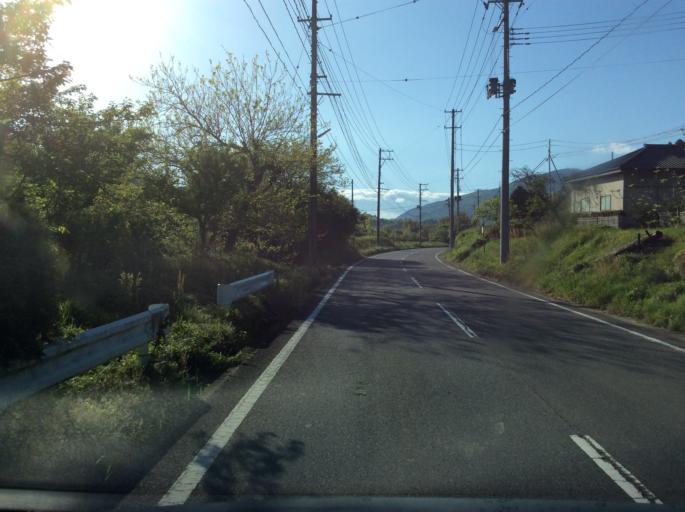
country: JP
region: Fukushima
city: Iwaki
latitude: 36.9869
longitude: 140.8324
